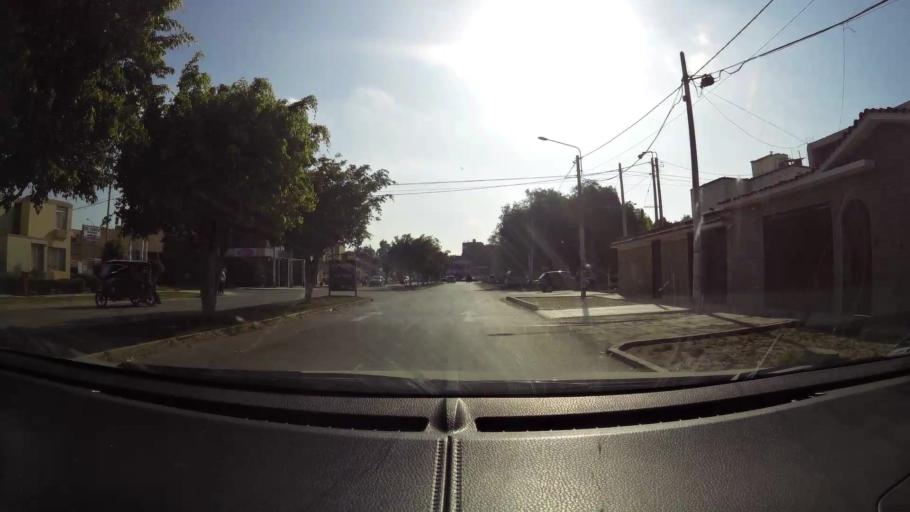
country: PE
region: Lambayeque
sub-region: Provincia de Chiclayo
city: Chiclayo
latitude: -6.7657
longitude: -79.8515
